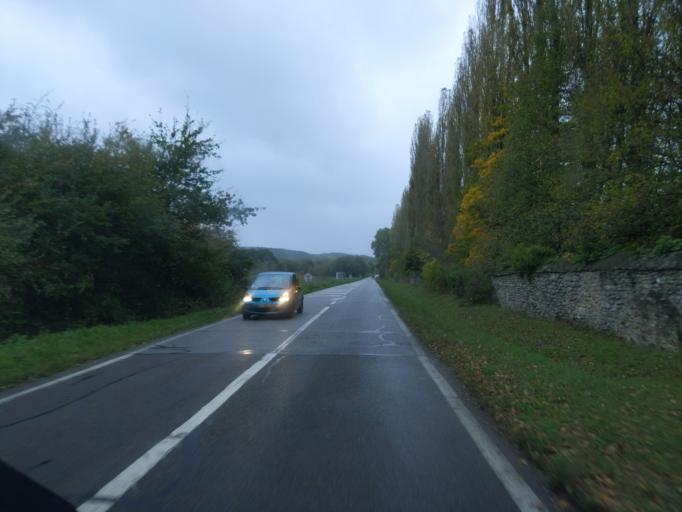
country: FR
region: Ile-de-France
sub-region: Departement des Yvelines
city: Dampierre-en-Yvelines
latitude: 48.6911
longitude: 1.9747
